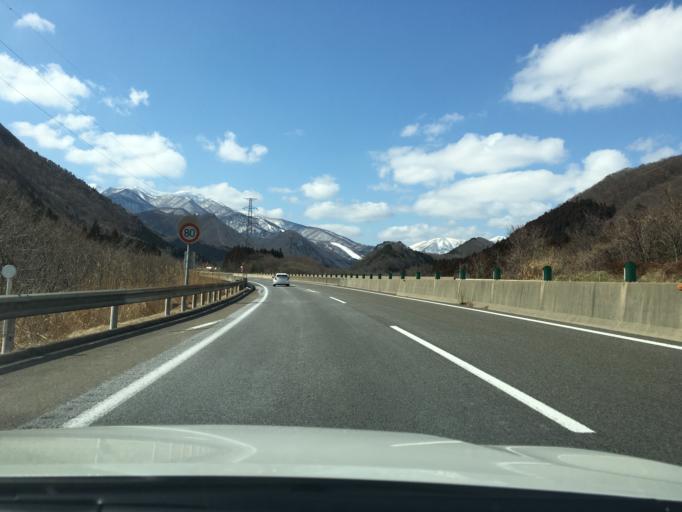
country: JP
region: Yamagata
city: Yamagata-shi
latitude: 38.2111
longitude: 140.5607
